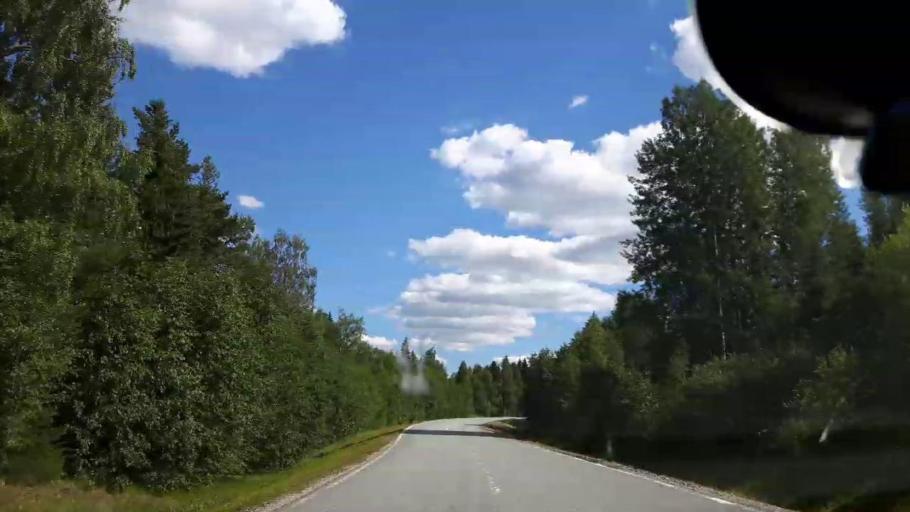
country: SE
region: Jaemtland
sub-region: Ragunda Kommun
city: Hammarstrand
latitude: 62.8317
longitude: 16.1805
